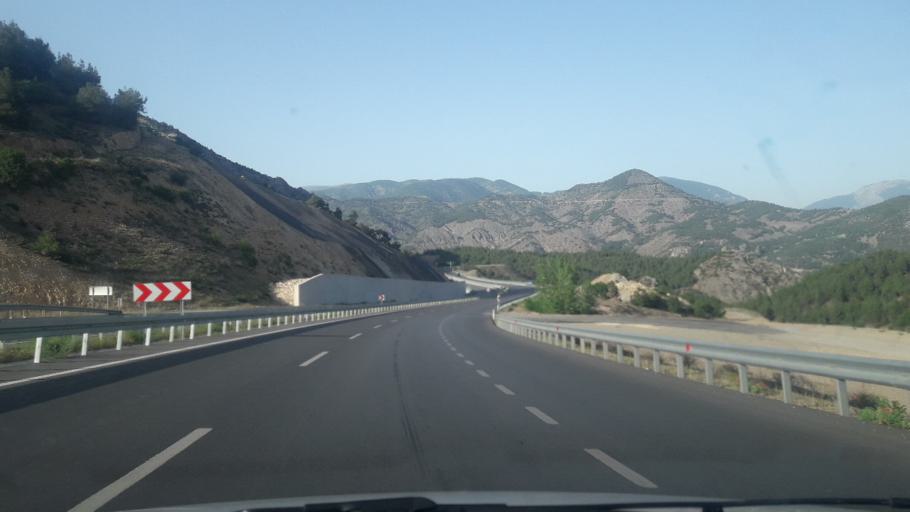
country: TR
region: Amasya
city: Amasya
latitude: 40.6769
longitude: 35.8048
